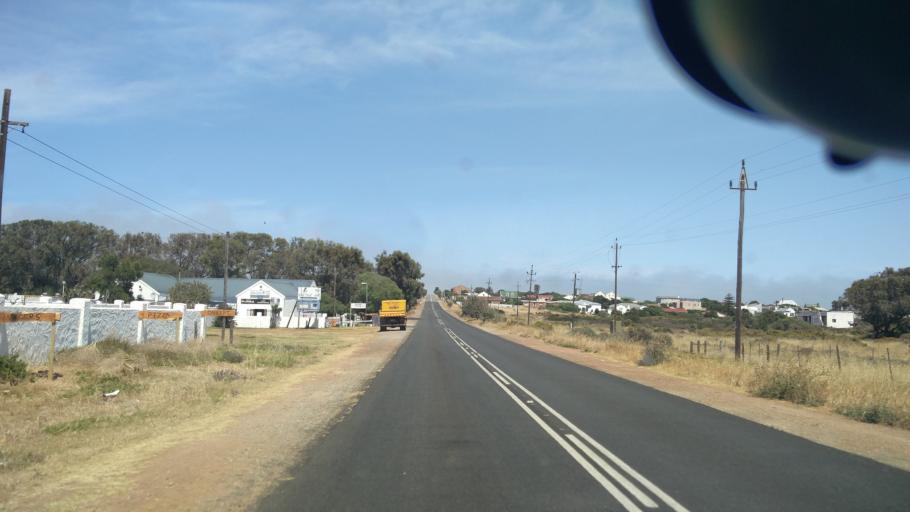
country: ZA
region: Western Cape
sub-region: City of Cape Town
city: Atlantis
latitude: -33.3428
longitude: 18.1724
